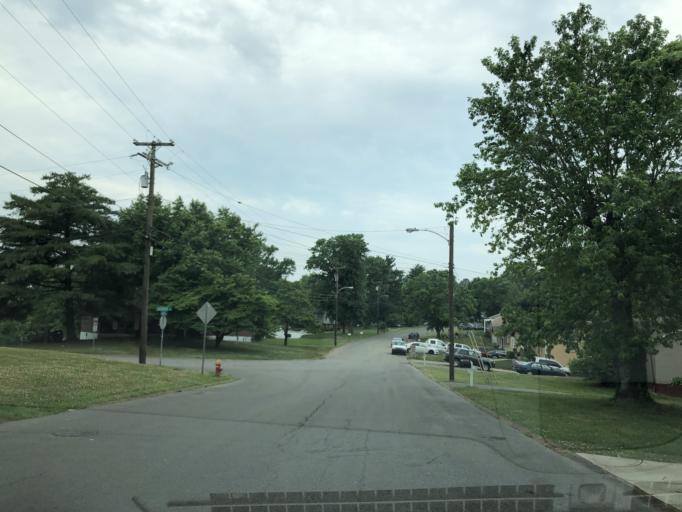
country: US
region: Tennessee
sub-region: Davidson County
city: Oak Hill
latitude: 36.0747
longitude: -86.6839
